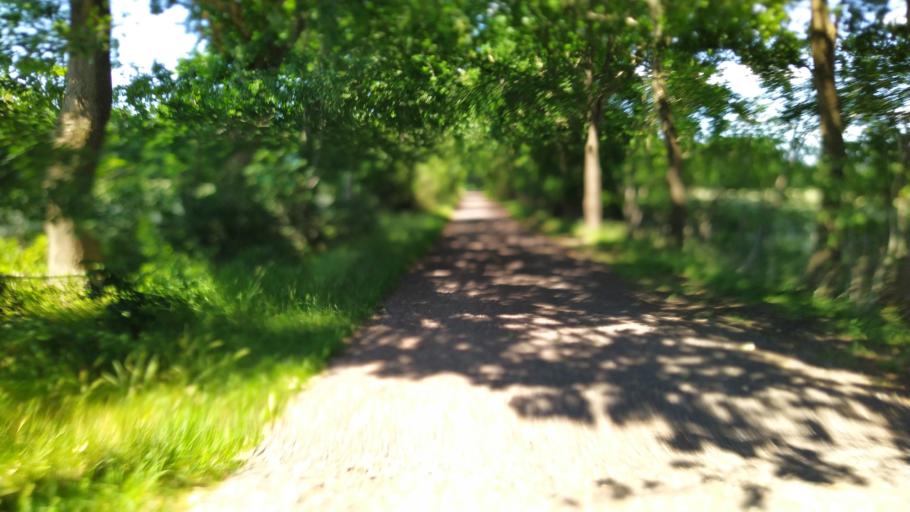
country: DE
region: Lower Saxony
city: Oldendorf
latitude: 53.5664
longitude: 9.2480
